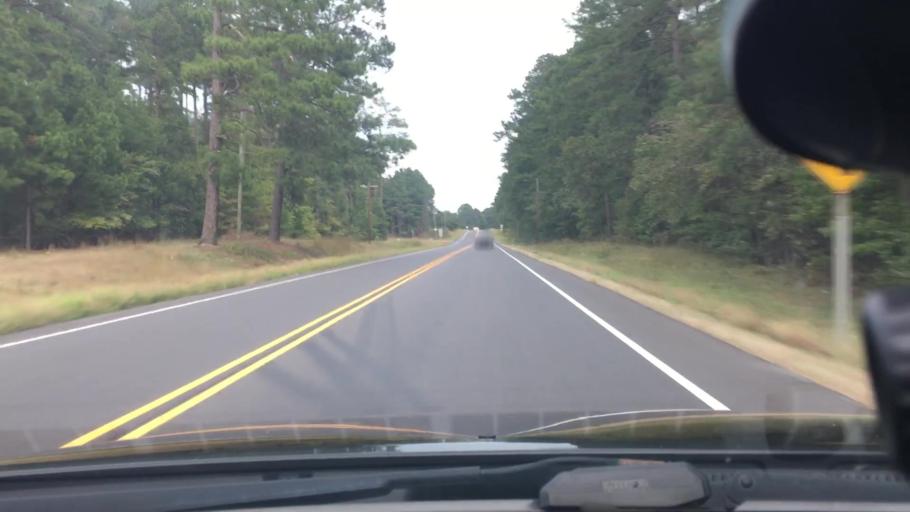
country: US
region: North Carolina
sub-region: Montgomery County
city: Biscoe
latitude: 35.3607
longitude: -79.7492
